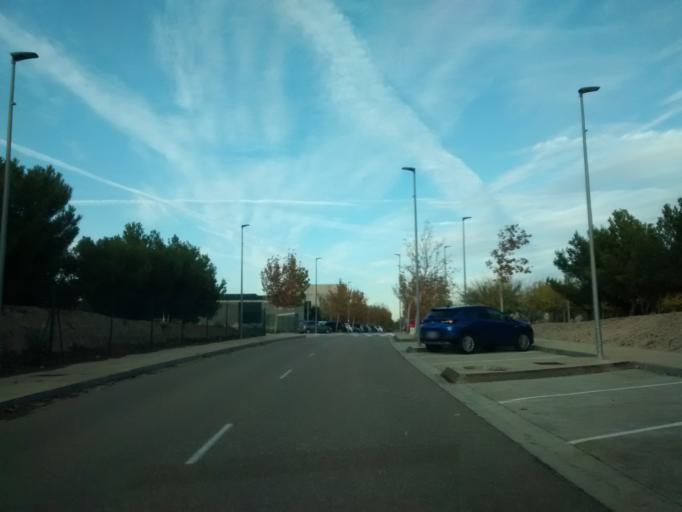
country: ES
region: Aragon
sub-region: Provincia de Zaragoza
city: Villanueva de Gallego
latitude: 41.7542
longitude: -0.8354
